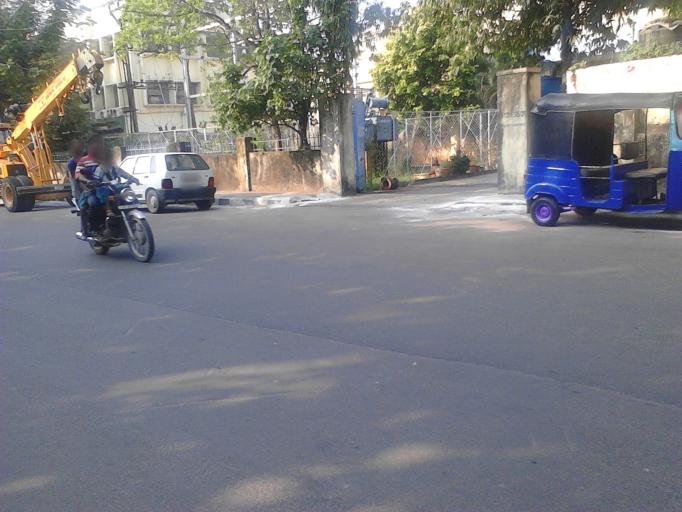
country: IN
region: Tamil Nadu
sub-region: Kancheepuram
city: Alandur
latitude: 13.0050
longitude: 80.2028
